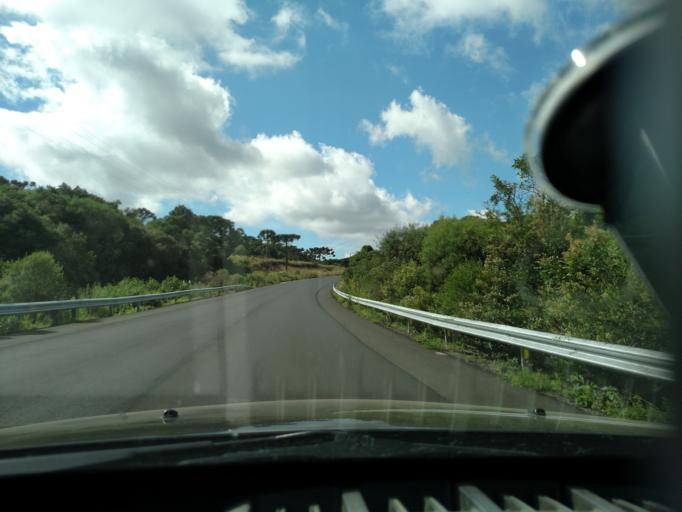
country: BR
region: Santa Catarina
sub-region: Lages
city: Lages
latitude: -27.9334
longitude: -50.0958
